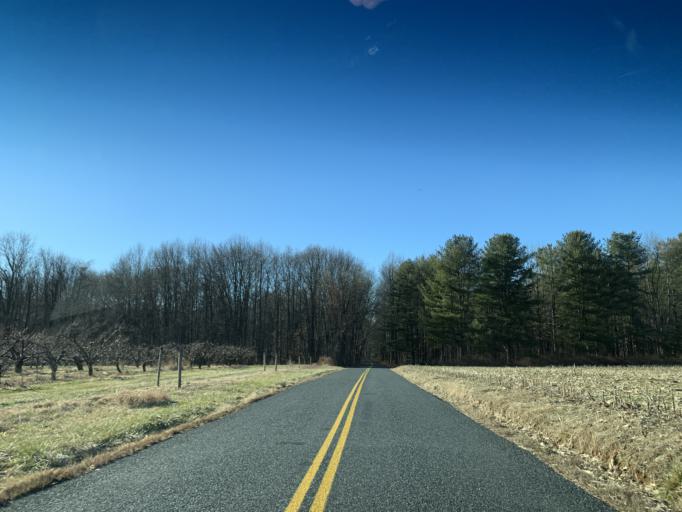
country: US
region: Maryland
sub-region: Harford County
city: Riverside
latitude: 39.5426
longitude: -76.2397
